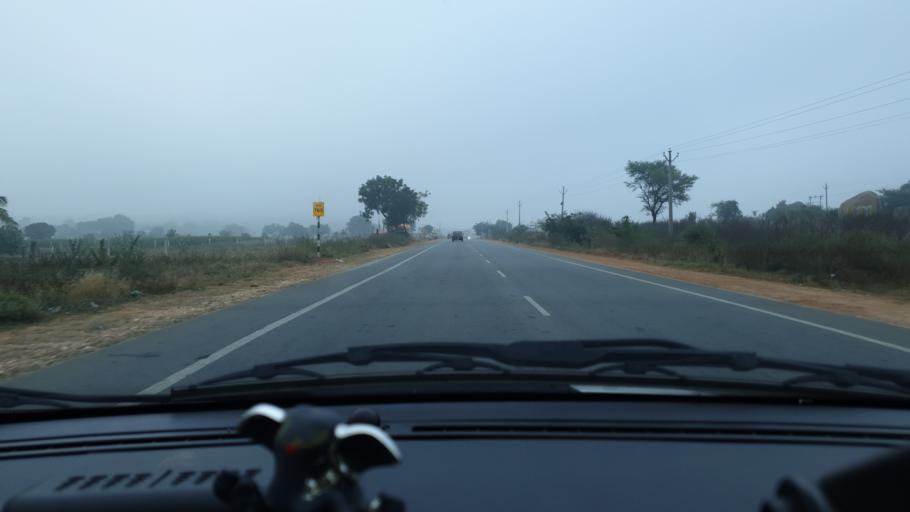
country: IN
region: Telangana
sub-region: Mahbubnagar
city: Farrukhnagar
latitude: 16.9408
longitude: 78.5266
